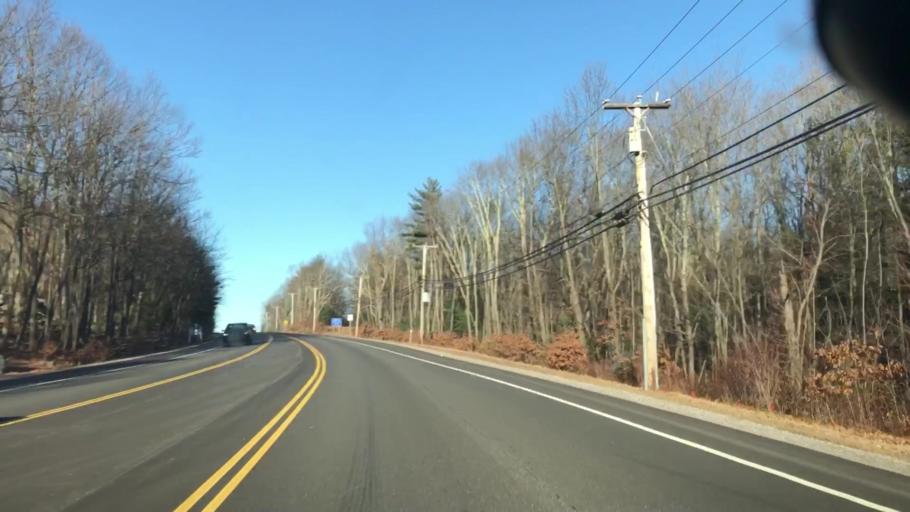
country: US
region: New Hampshire
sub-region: Hillsborough County
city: Bedford
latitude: 42.9235
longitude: -71.5354
